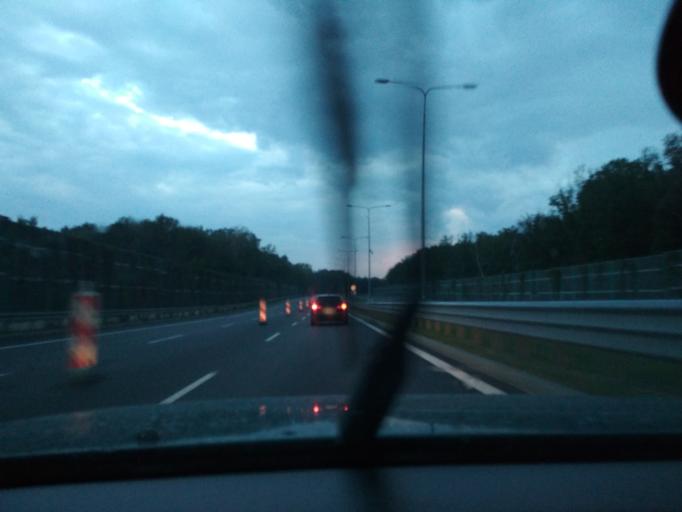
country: PL
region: Silesian Voivodeship
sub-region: Zabrze
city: Zabrze
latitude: 50.2862
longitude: 18.7745
